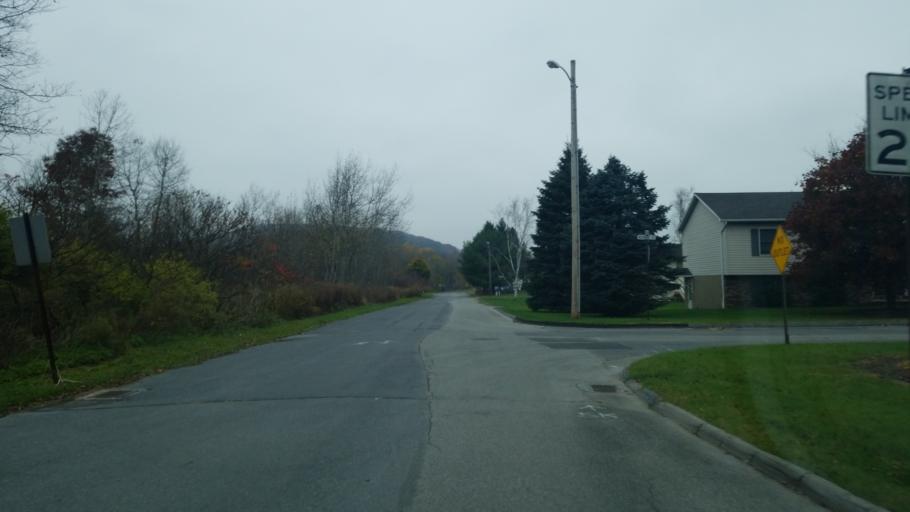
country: US
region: Pennsylvania
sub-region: Clearfield County
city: Clearfield
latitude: 41.0064
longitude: -78.4408
